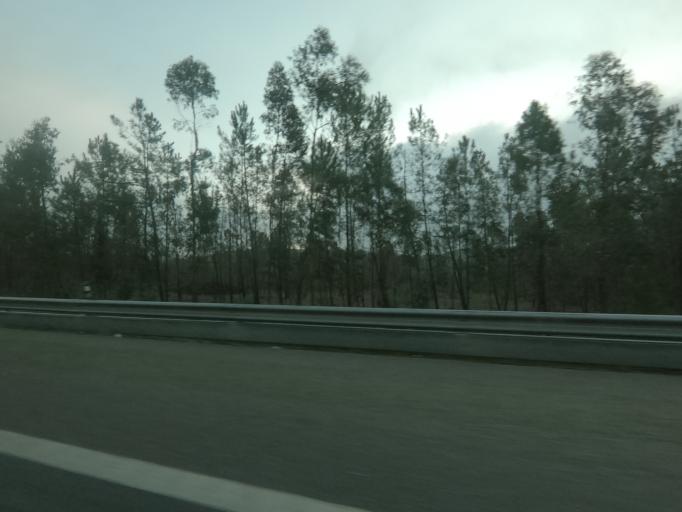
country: PT
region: Braga
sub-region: Barcelos
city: Galegos
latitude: 41.6486
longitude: -8.5515
